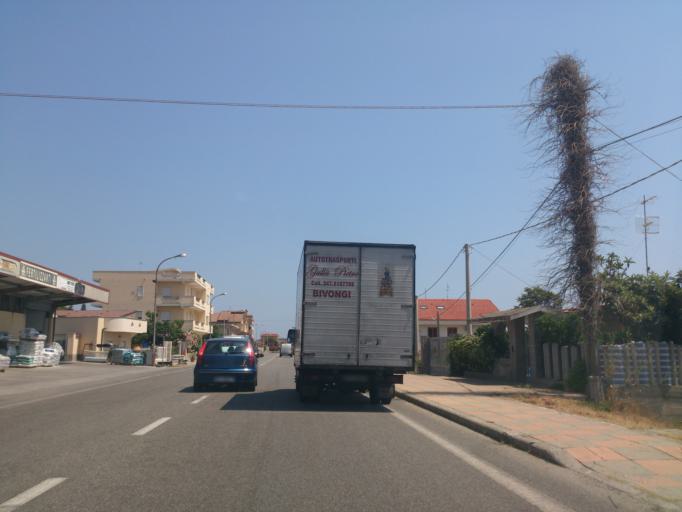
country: IT
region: Calabria
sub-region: Provincia di Reggio Calabria
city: Riace Marina
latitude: 38.3956
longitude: 16.5362
